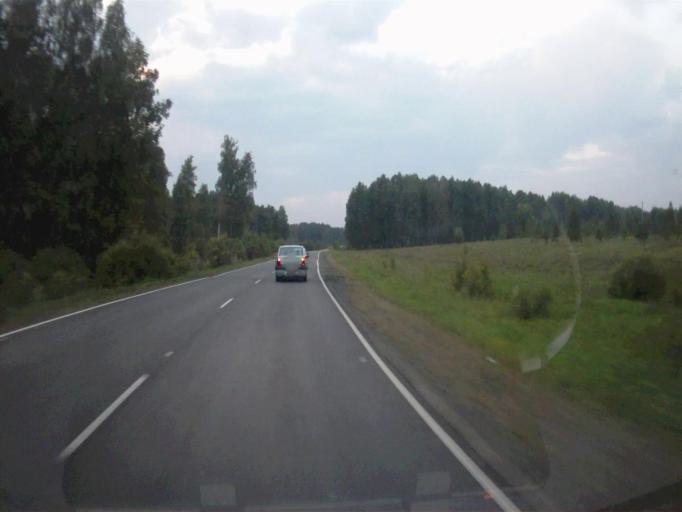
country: RU
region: Chelyabinsk
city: Chebarkul'
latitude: 55.1840
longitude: 60.4673
